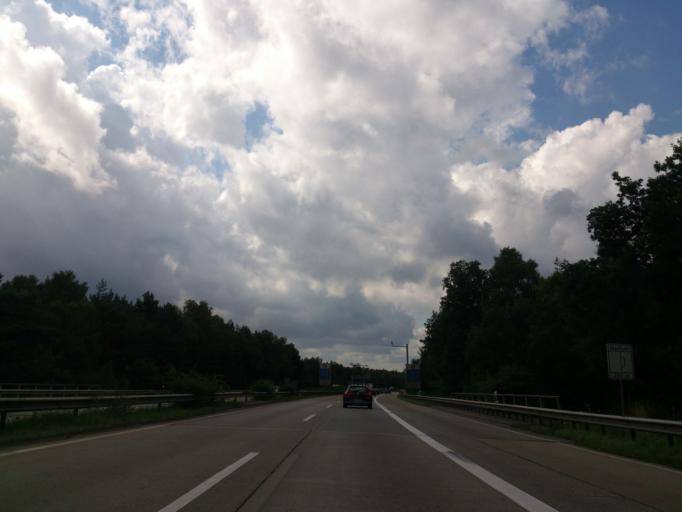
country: DE
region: Lower Saxony
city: Soltau
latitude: 52.9870
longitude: 9.9289
